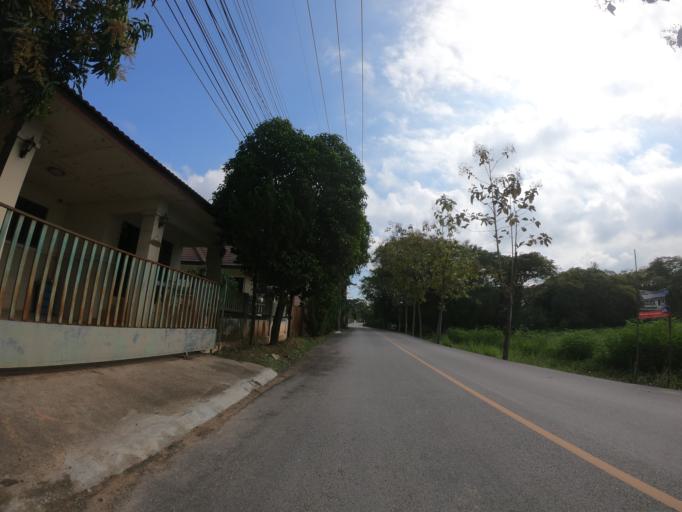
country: TH
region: Chiang Mai
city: San Sai
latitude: 18.8632
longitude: 99.0247
